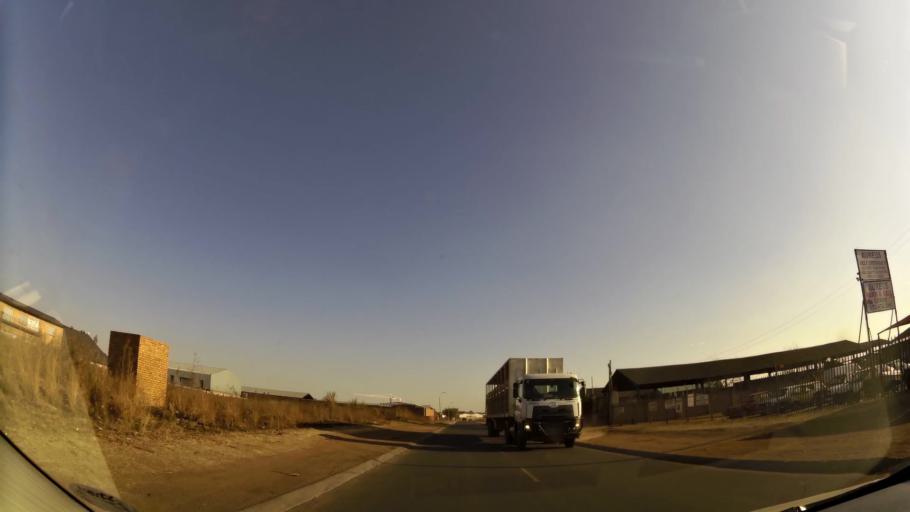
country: ZA
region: Gauteng
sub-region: West Rand District Municipality
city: Randfontein
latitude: -26.1970
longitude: 27.6894
